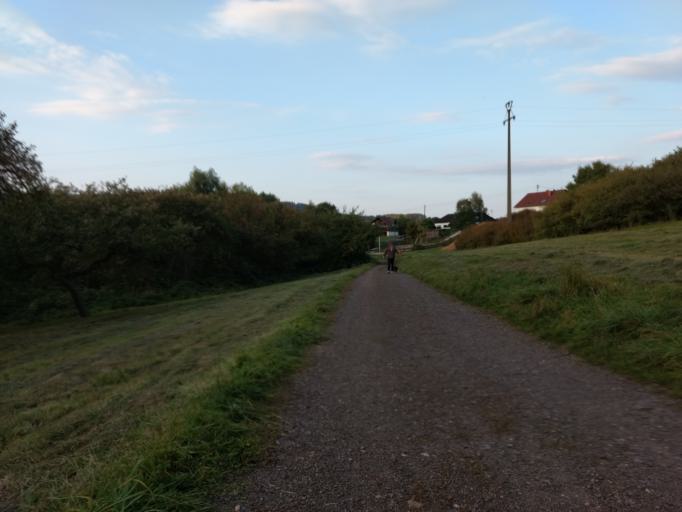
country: DE
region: Saarland
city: Nalbach
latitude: 49.3855
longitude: 6.7854
